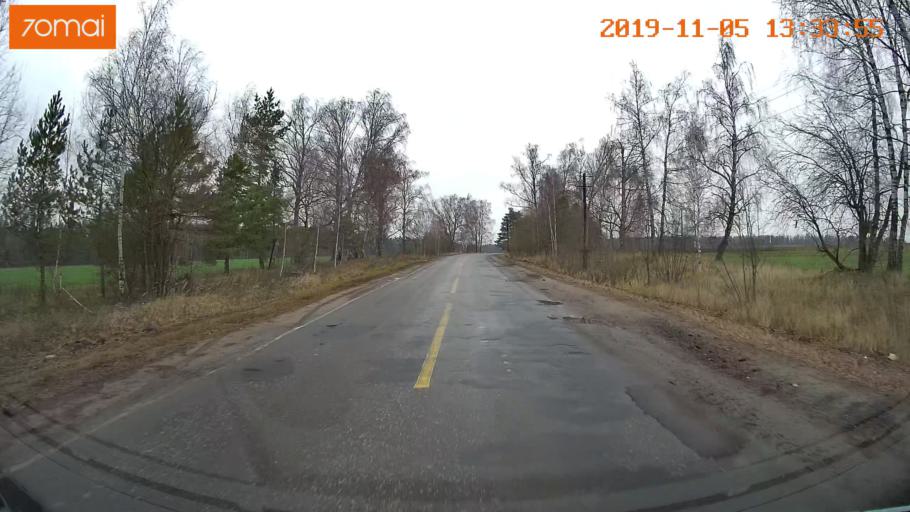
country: RU
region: Ivanovo
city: Shuya
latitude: 56.8963
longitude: 41.3907
